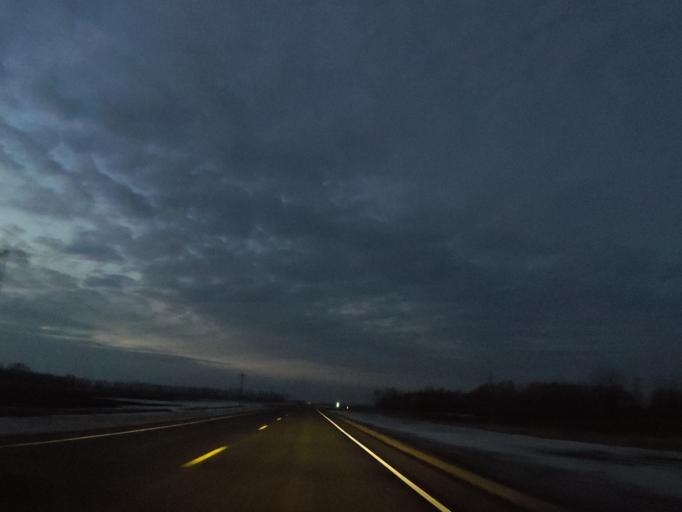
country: US
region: North Dakota
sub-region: Walsh County
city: Park River
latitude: 48.2893
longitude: -97.6225
